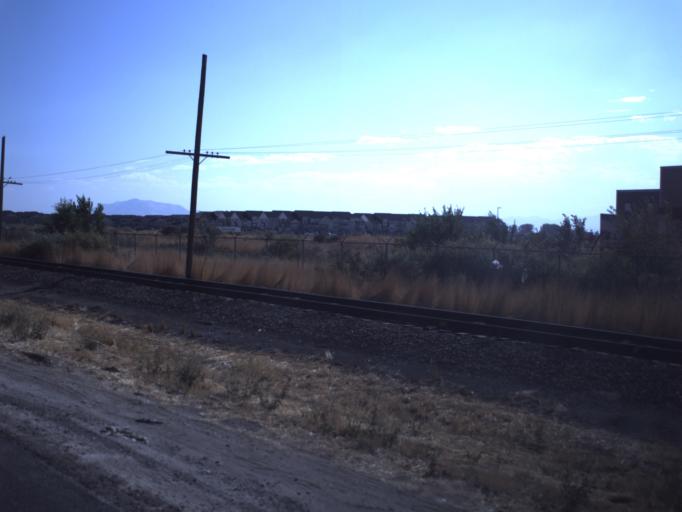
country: US
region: Utah
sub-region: Utah County
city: Lindon
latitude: 40.3080
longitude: -111.7341
